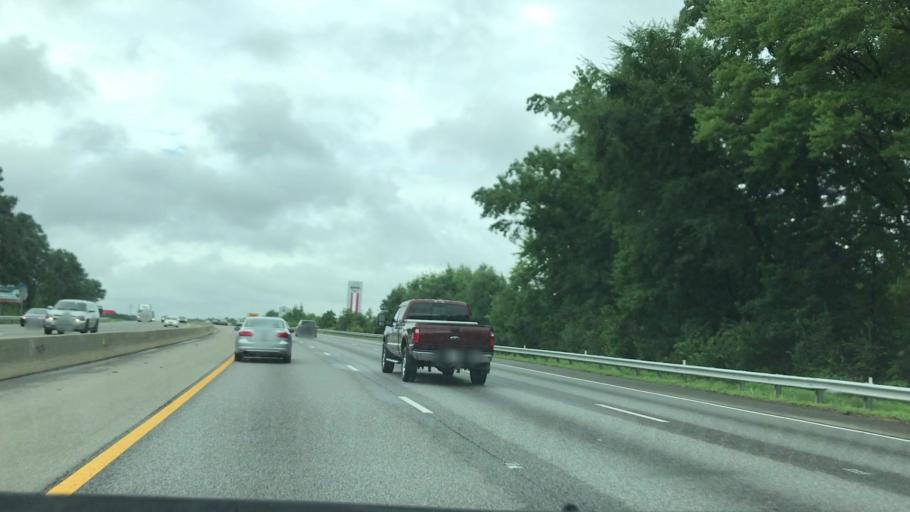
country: US
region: Virginia
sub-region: City of Colonial Heights
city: Colonial Heights
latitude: 37.3023
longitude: -77.3920
